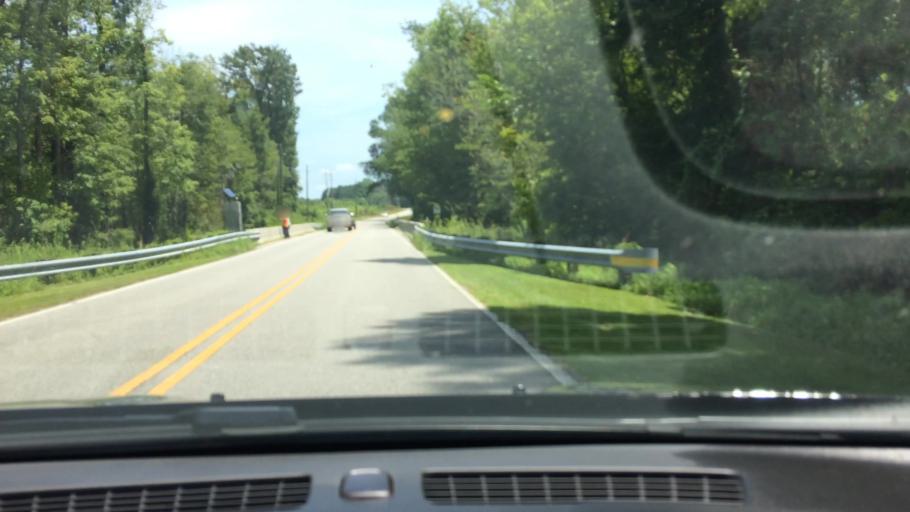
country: US
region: North Carolina
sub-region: Pitt County
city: Windsor
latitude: 35.5613
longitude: -77.2313
